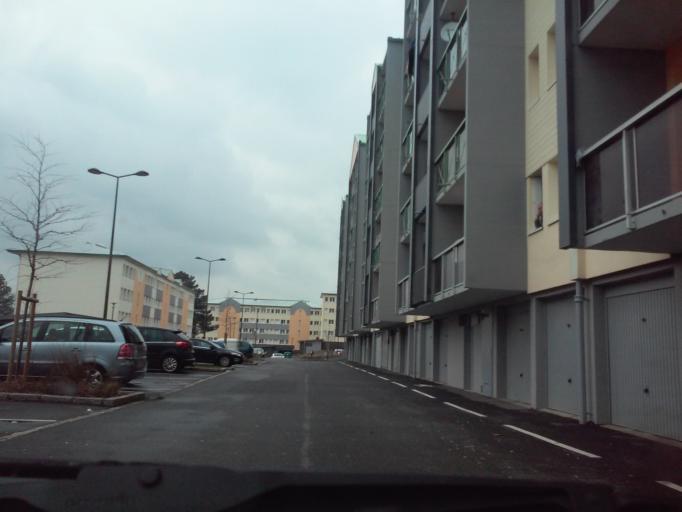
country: FR
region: Brittany
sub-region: Departement d'Ille-et-Vilaine
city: Fougeres
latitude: 48.3662
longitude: -1.1823
